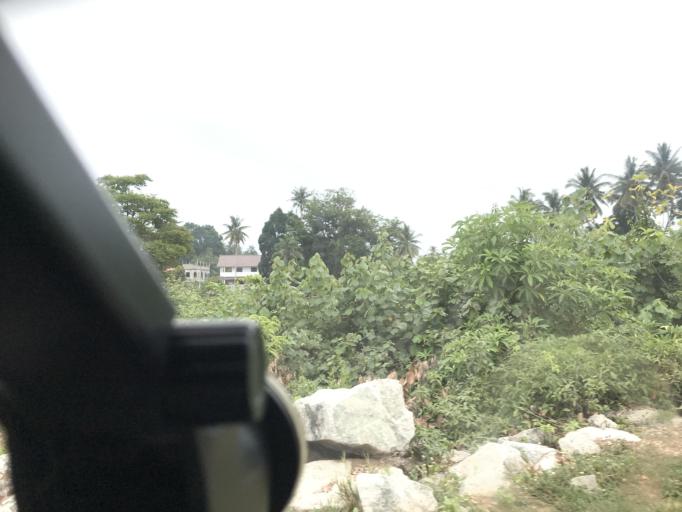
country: MY
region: Kelantan
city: Tumpat
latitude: 6.1737
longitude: 102.2046
